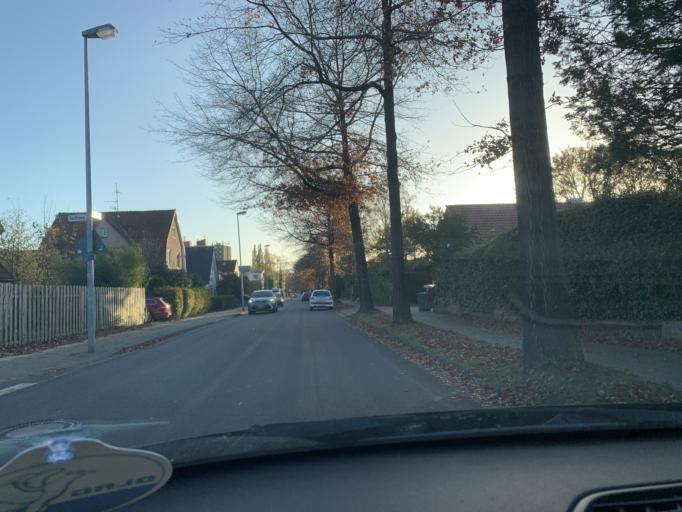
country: DE
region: Lower Saxony
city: Oldenburg
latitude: 53.1435
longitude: 8.1773
